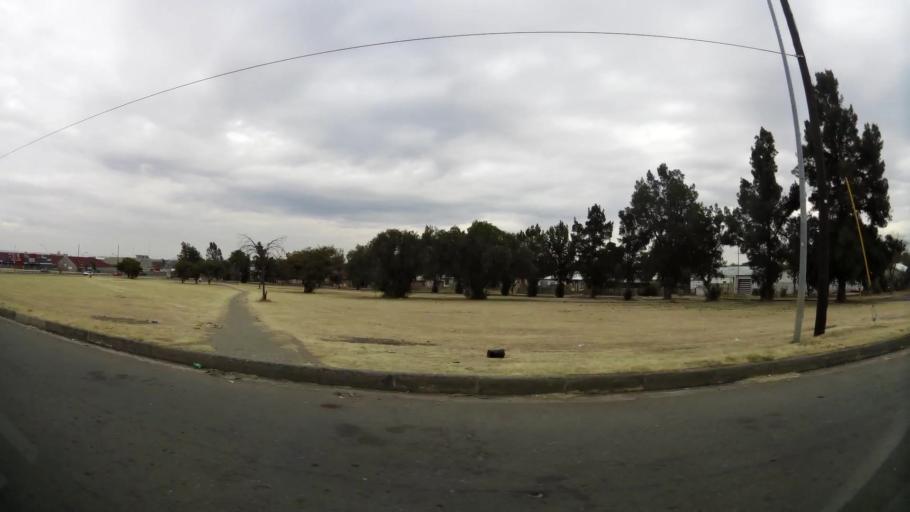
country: ZA
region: Orange Free State
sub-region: Fezile Dabi District Municipality
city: Kroonstad
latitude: -27.6482
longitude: 27.2312
